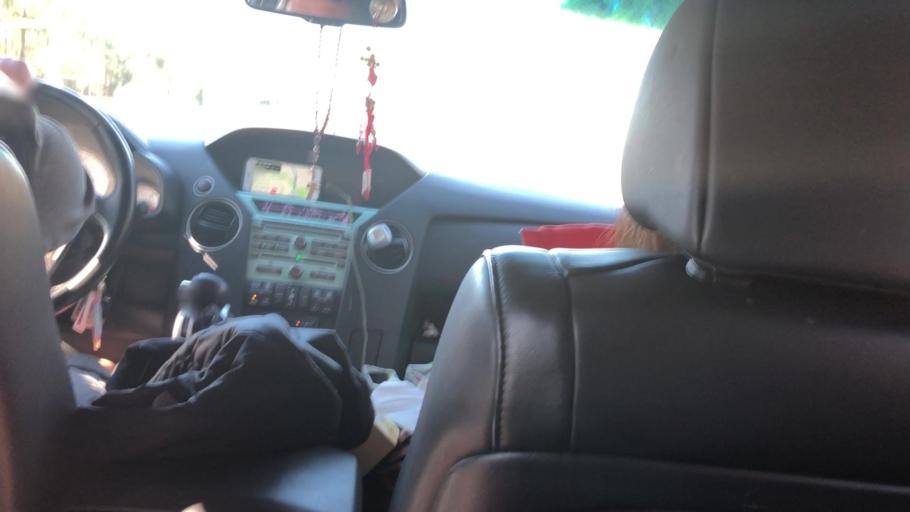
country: US
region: Louisiana
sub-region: Saint John the Baptist Parish
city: Montegut
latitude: 30.1027
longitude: -90.4883
